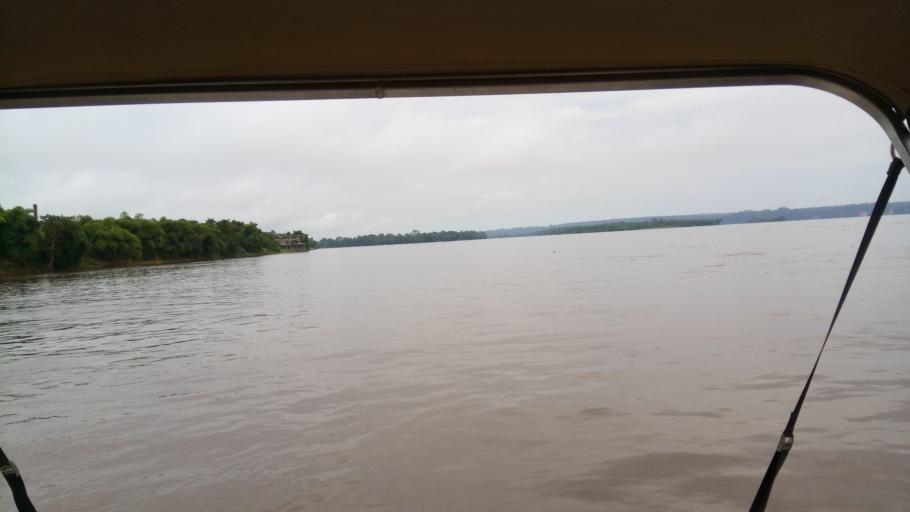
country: CD
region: Eastern Province
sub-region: Sous-Region de la Tshopo
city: Yangambi
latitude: 0.7141
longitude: 24.5631
